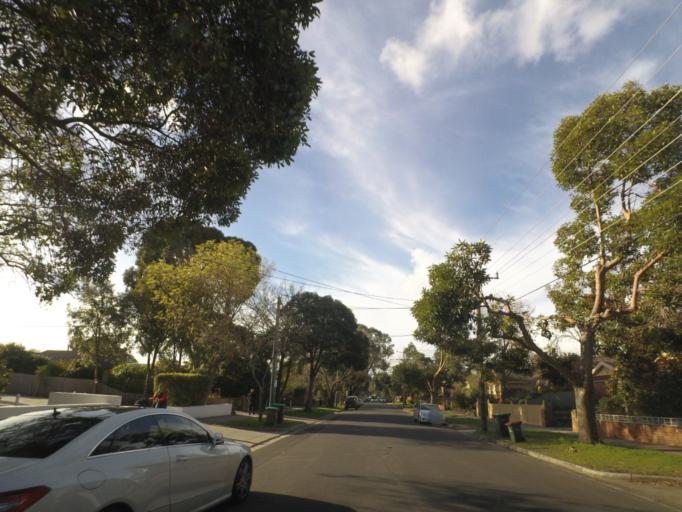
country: AU
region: Victoria
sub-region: Whitehorse
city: Blackburn South
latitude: -37.8308
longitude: 145.1486
